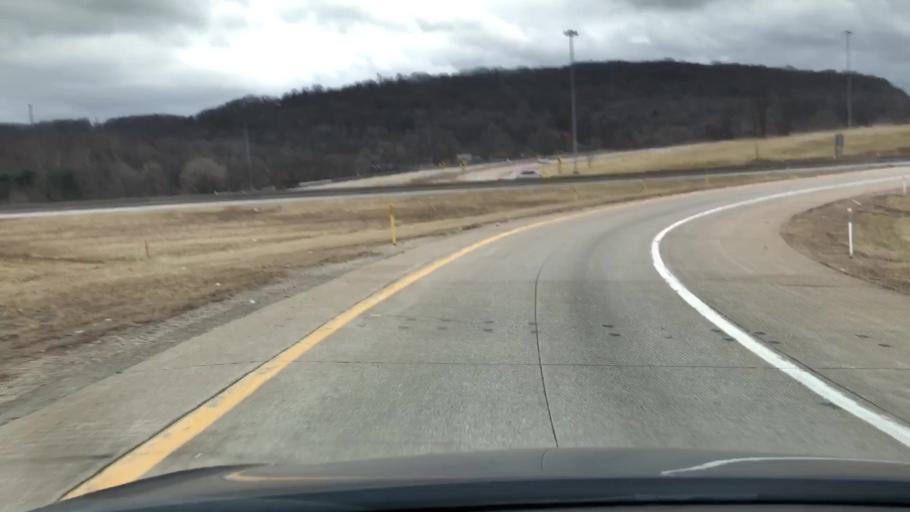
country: US
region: Pennsylvania
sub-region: Westmoreland County
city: New Stanton
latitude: 40.2274
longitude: -79.5927
